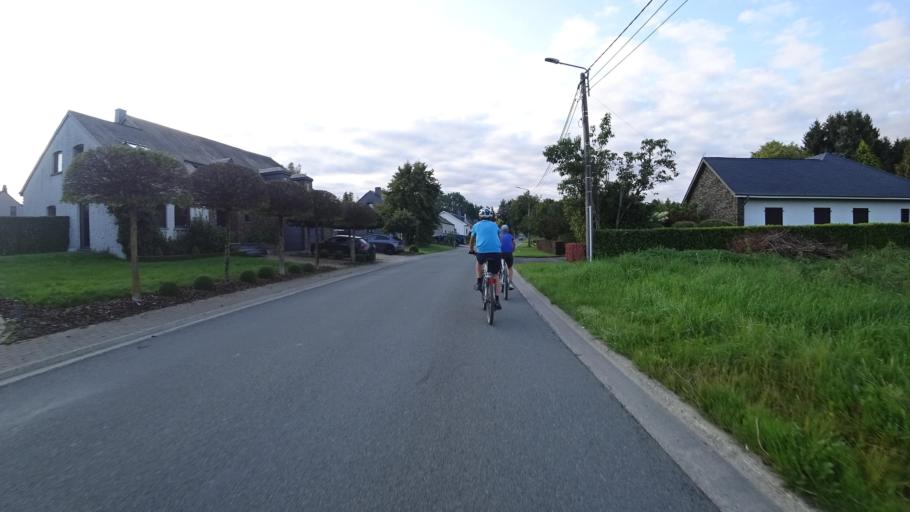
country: BE
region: Wallonia
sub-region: Province du Luxembourg
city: Neufchateau
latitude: 49.9095
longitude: 5.3850
